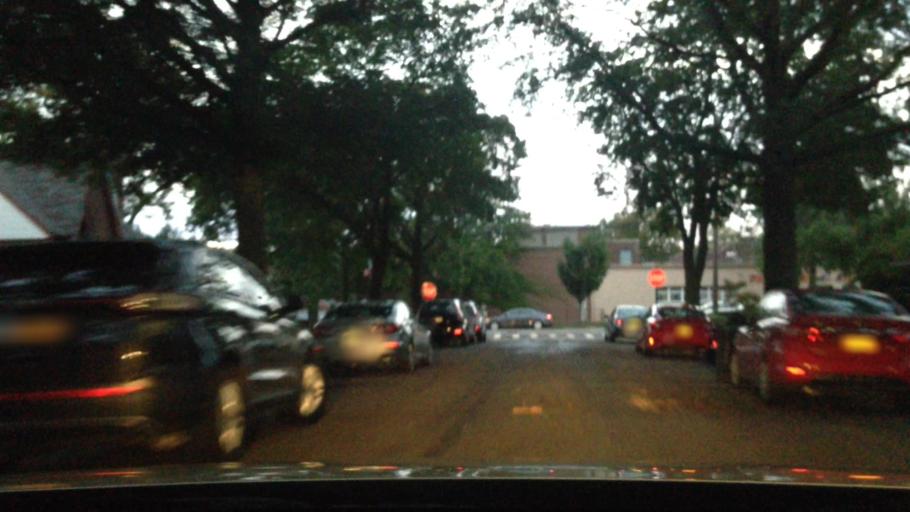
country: US
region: New York
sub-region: Queens County
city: Jamaica
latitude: 40.7320
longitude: -73.7846
